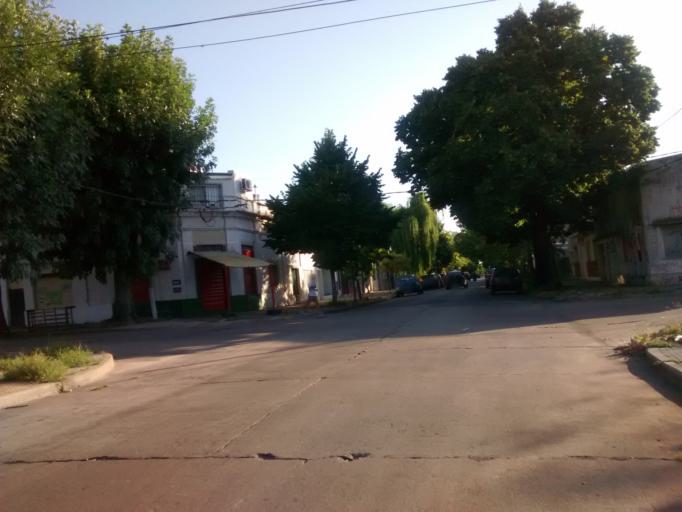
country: AR
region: Buenos Aires
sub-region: Partido de La Plata
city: La Plata
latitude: -34.9176
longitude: -57.9297
